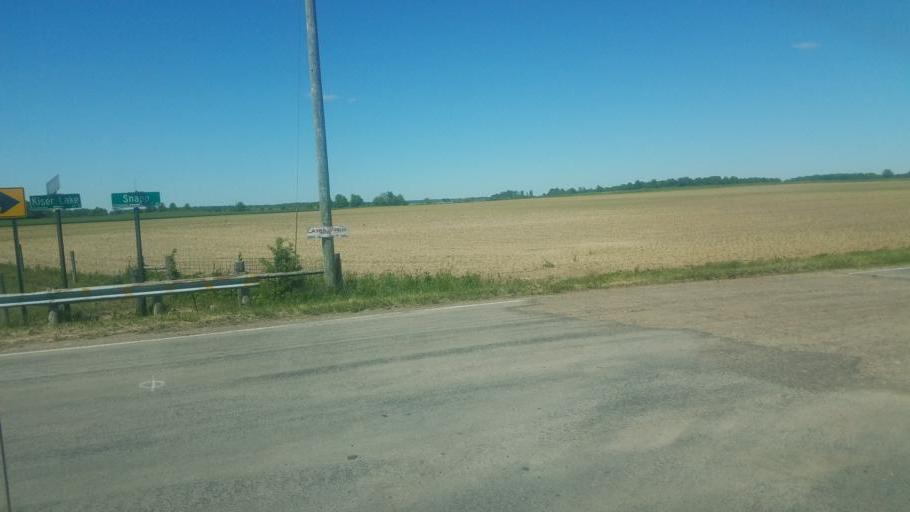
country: US
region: Ohio
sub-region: Champaign County
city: Saint Paris
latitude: 40.1966
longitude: -83.9537
